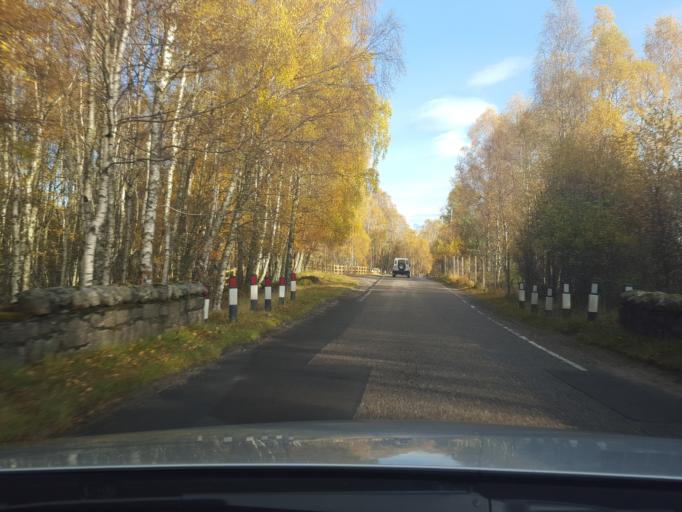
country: GB
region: Scotland
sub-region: Highland
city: Spean Bridge
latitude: 57.1718
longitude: -4.8102
